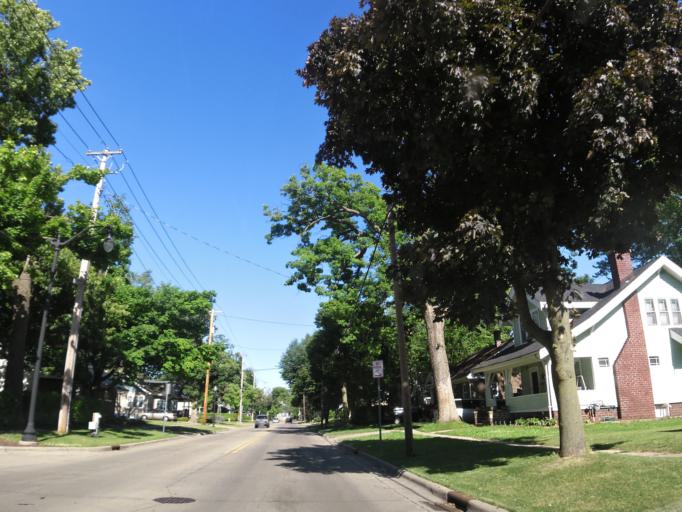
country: US
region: Wisconsin
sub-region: Rock County
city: Beloit
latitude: 42.5109
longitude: -89.0171
